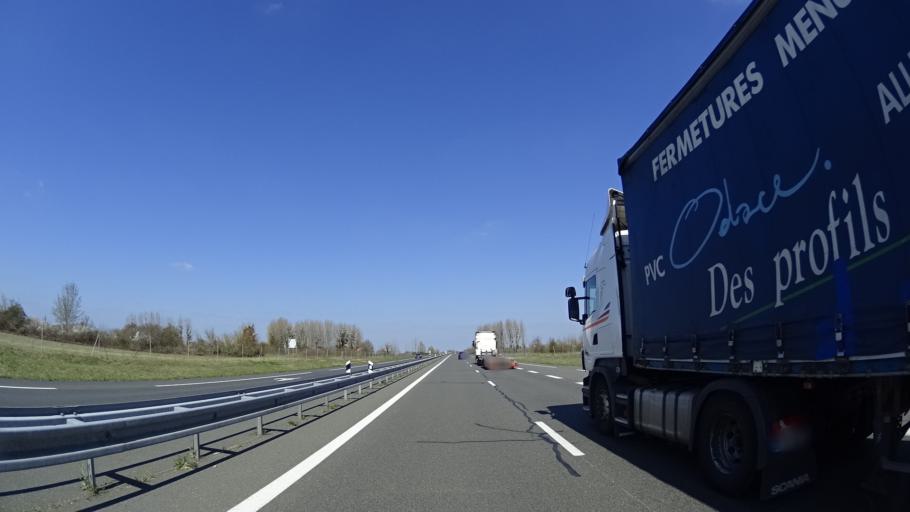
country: FR
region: Pays de la Loire
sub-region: Departement de Maine-et-Loire
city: Saint-Jean
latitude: 47.2586
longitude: -0.3337
